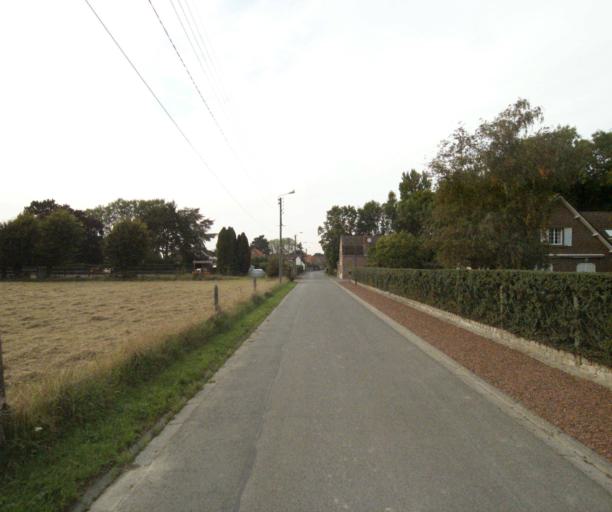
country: FR
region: Nord-Pas-de-Calais
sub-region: Departement du Nord
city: Seclin
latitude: 50.5305
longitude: 3.0327
